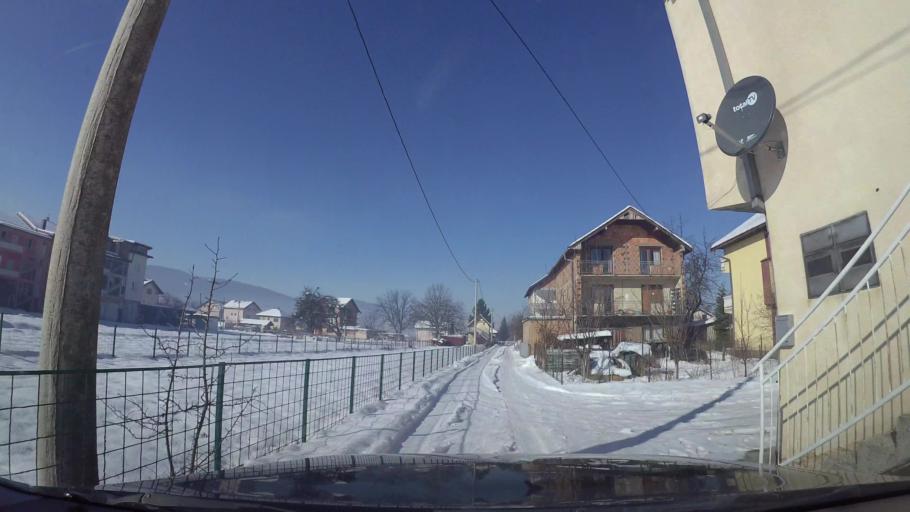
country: BA
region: Federation of Bosnia and Herzegovina
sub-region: Kanton Sarajevo
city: Sarajevo
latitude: 43.8131
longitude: 18.3537
